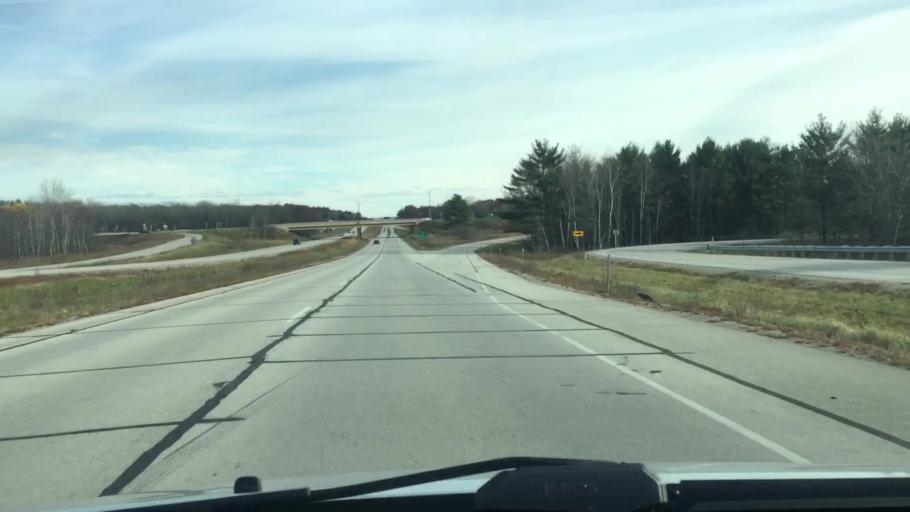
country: US
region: Wisconsin
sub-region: Brown County
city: Howard
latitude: 44.5623
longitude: -88.1353
